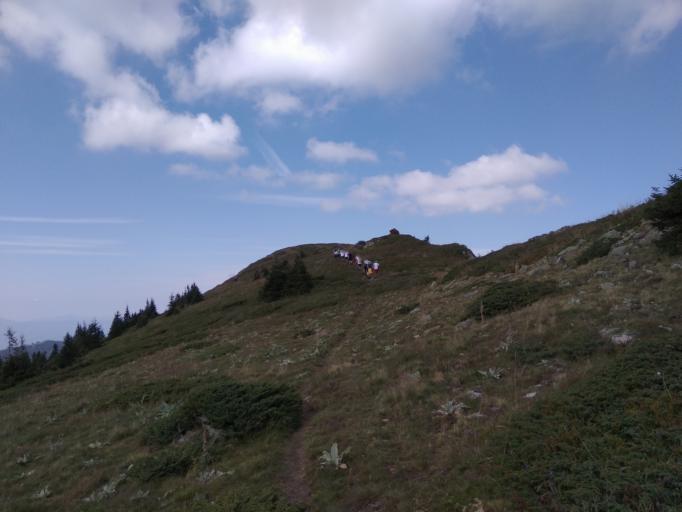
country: BG
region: Plovdiv
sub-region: Obshtina Karlovo
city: Karlovo
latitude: 42.7293
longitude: 24.7512
